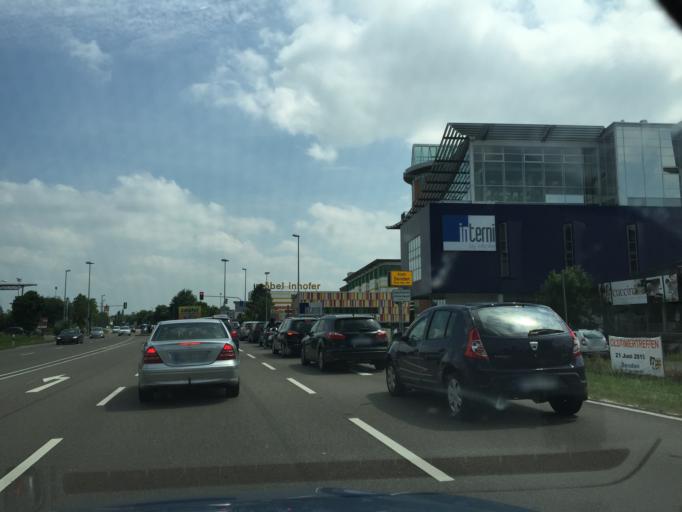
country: DE
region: Bavaria
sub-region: Swabia
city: Senden
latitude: 48.3308
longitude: 10.0370
